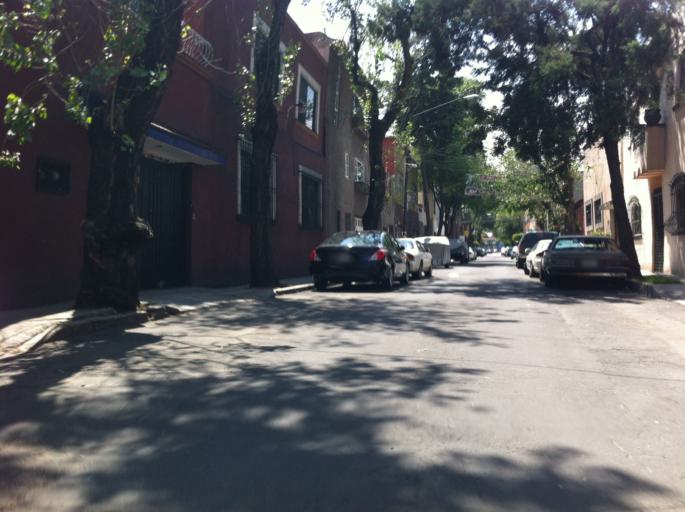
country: MX
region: Mexico City
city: Colonia del Valle
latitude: 19.3938
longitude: -99.1837
